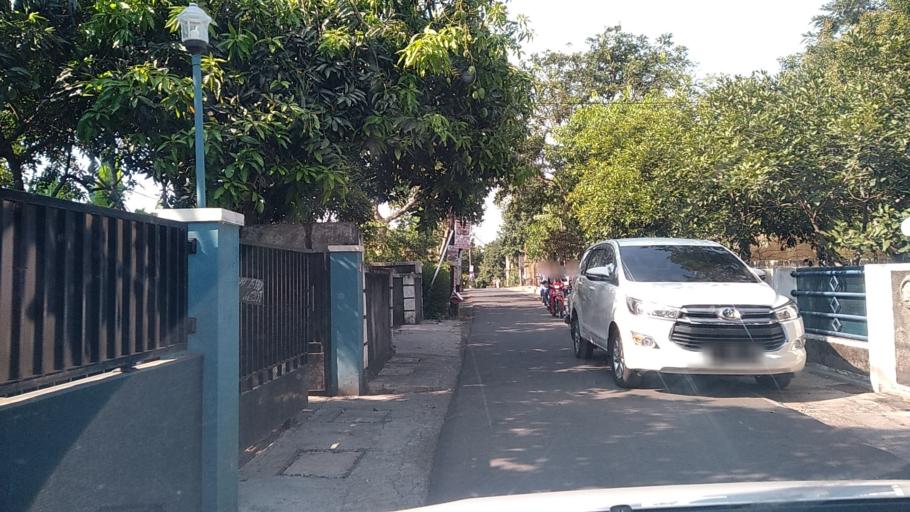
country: ID
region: Central Java
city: Semarang
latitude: -7.0614
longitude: 110.4210
